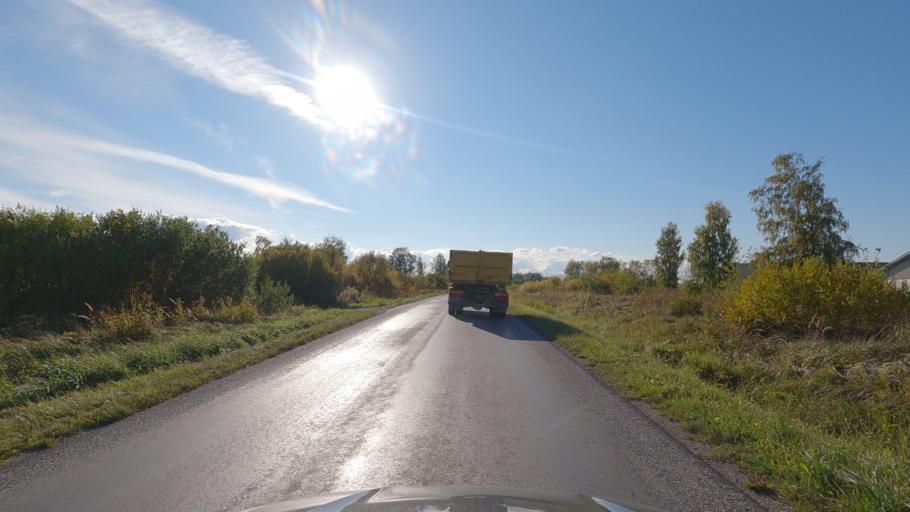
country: EE
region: Harju
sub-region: Joelaehtme vald
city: Loo
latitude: 59.4203
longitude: 24.9735
